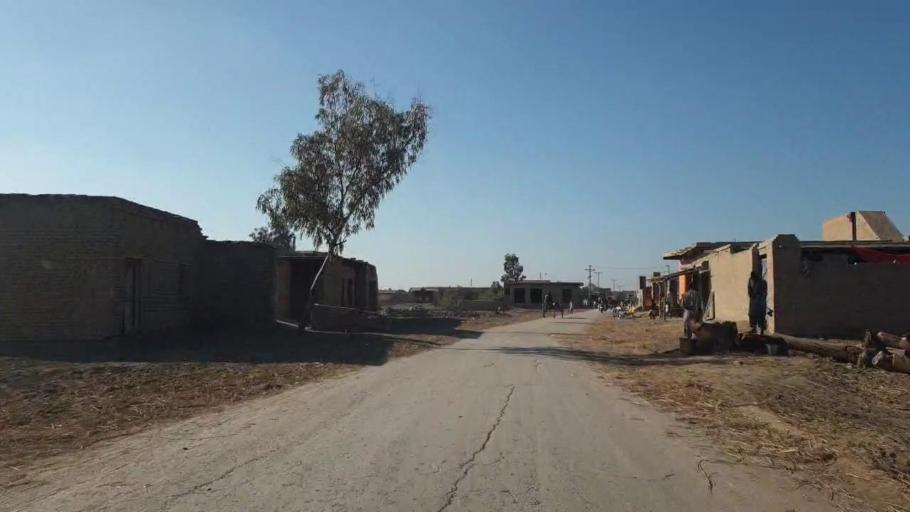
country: PK
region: Sindh
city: New Badah
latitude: 27.3248
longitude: 68.0324
